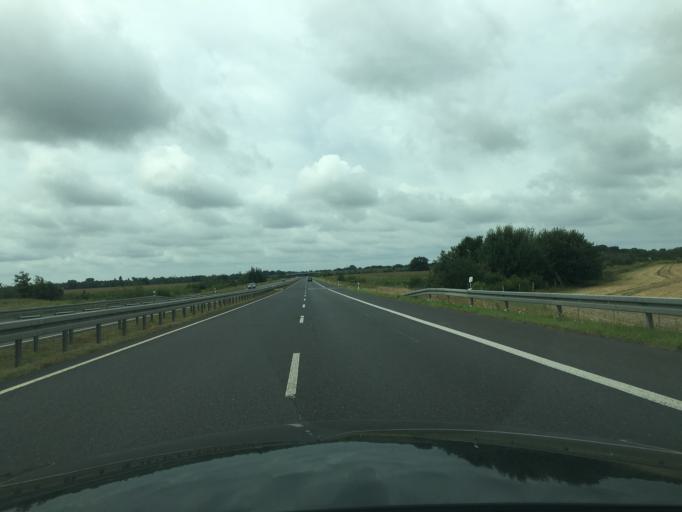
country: DE
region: Brandenburg
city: Oranienburg
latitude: 52.7737
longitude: 13.2172
